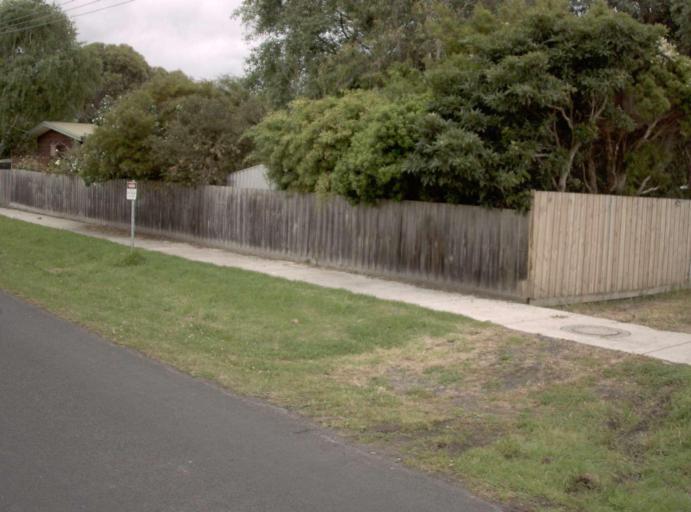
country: AU
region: Victoria
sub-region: Bass Coast
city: North Wonthaggi
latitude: -38.5968
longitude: 145.6060
